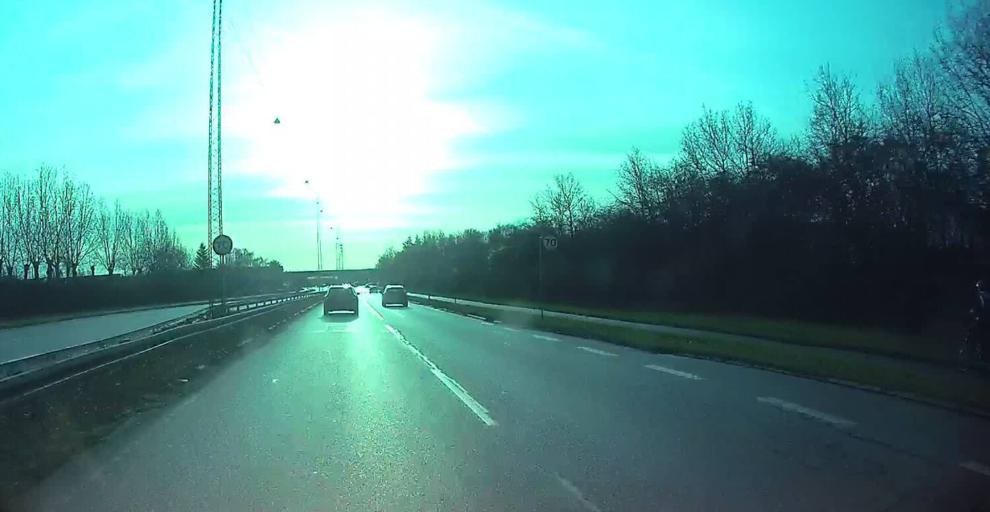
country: DK
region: Capital Region
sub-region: Hvidovre Kommune
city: Hvidovre
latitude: 55.6289
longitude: 12.4712
